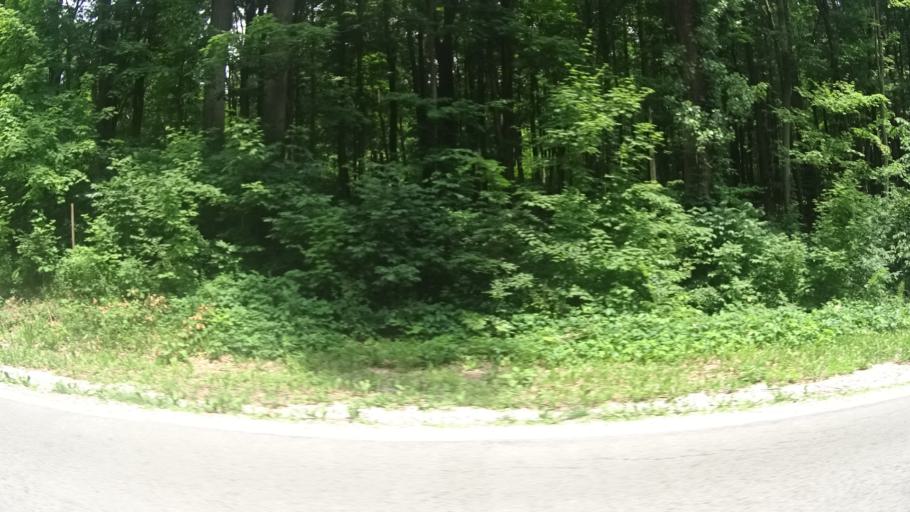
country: US
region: Ohio
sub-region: Erie County
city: Milan
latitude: 41.2892
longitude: -82.6448
